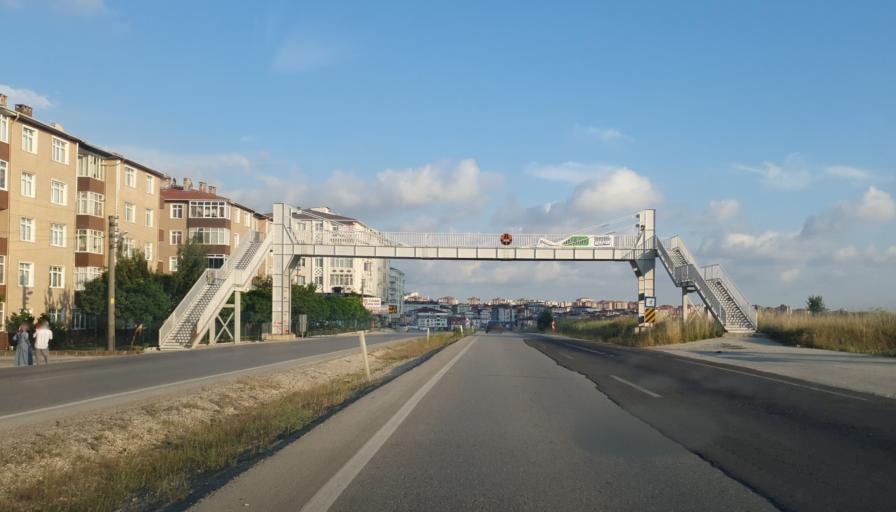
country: TR
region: Tekirdag
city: Cerkezkoey
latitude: 41.3351
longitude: 27.9682
